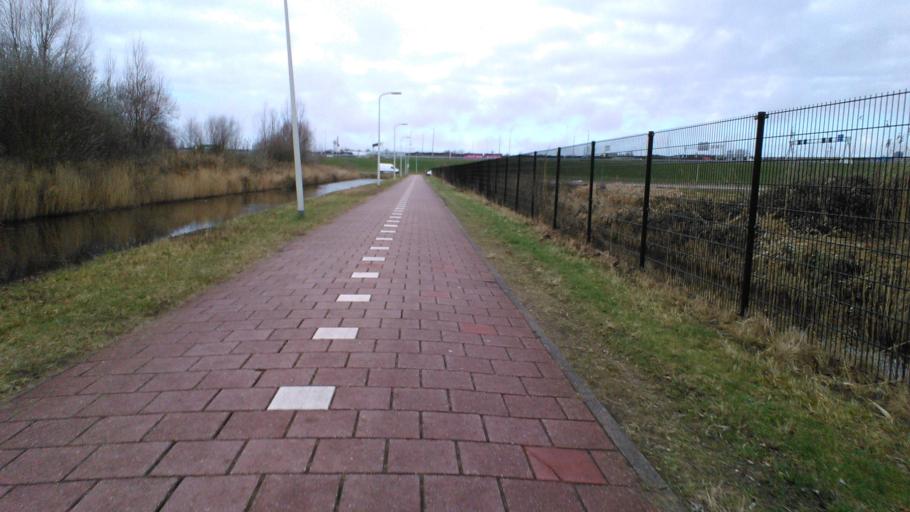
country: NL
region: South Holland
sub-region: Gemeente Den Haag
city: Ypenburg
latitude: 52.0570
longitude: 4.3744
